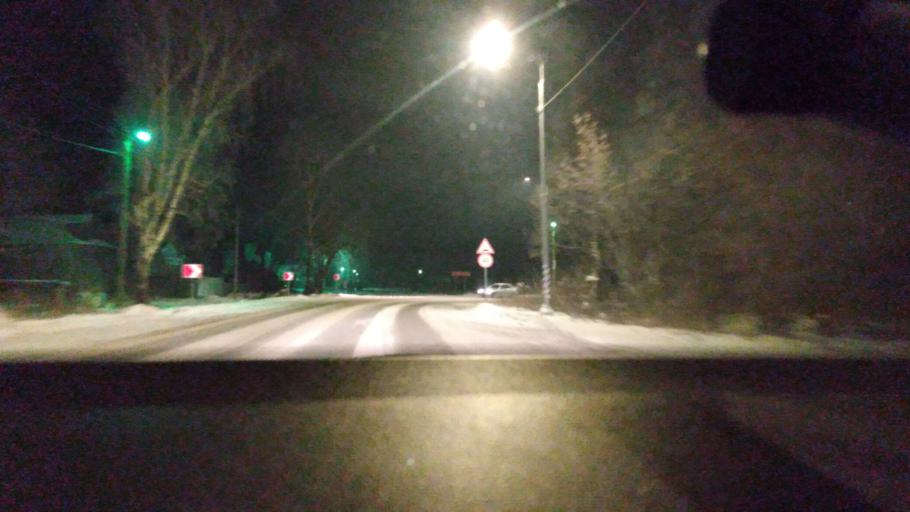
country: RU
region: Moskovskaya
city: Krasnaya Poyma
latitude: 55.1301
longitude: 39.0946
